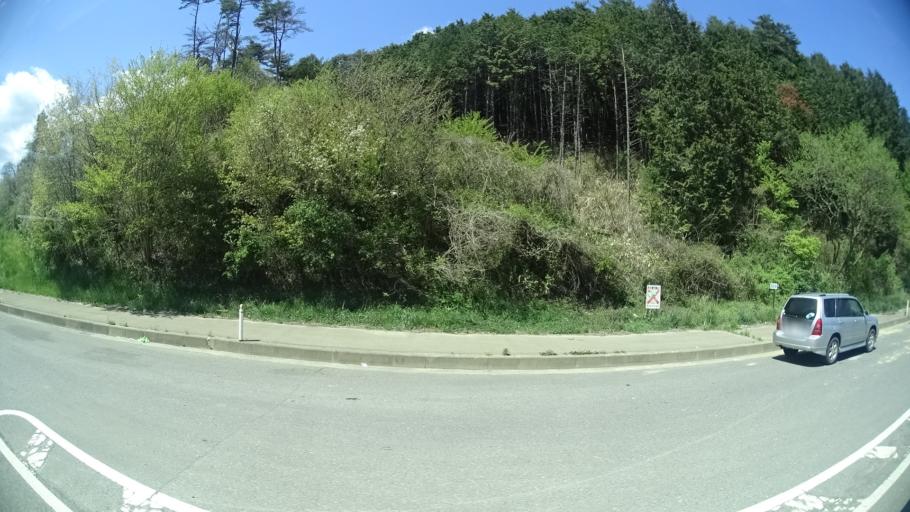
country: JP
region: Miyagi
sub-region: Oshika Gun
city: Onagawa Cho
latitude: 38.6920
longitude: 141.4725
